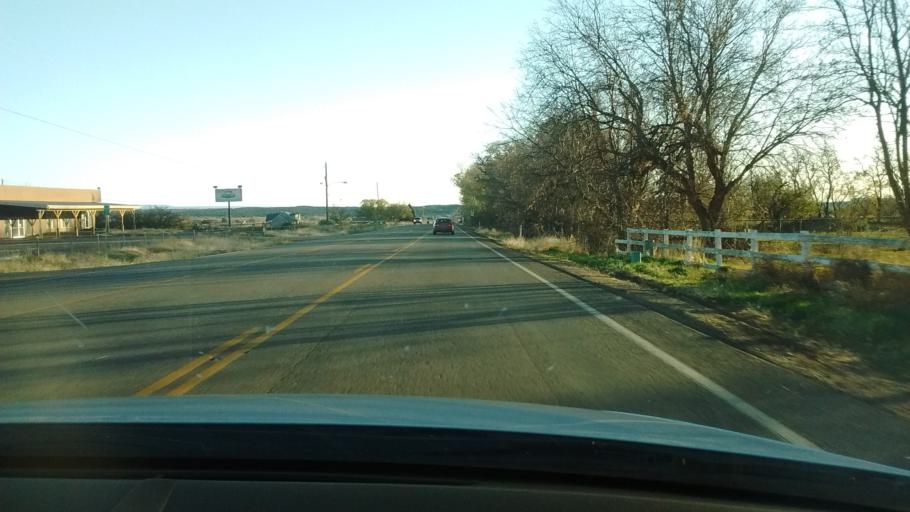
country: US
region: Utah
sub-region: Kane County
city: Kanab
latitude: 37.0297
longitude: -112.5249
